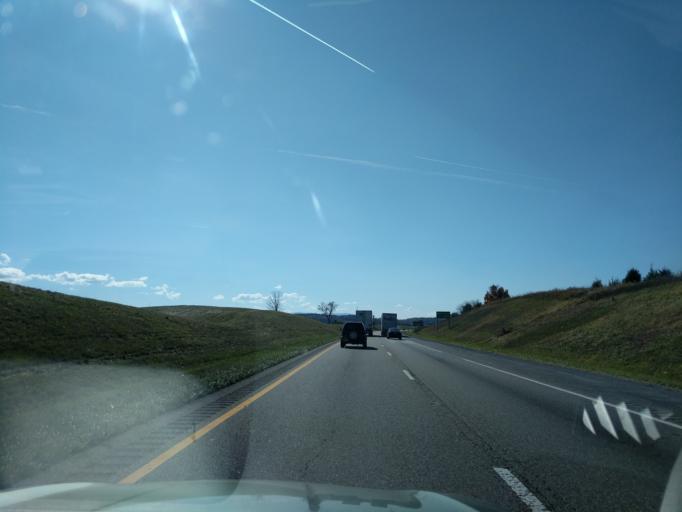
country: US
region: Virginia
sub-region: Augusta County
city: Verona
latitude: 38.1775
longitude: -79.0013
